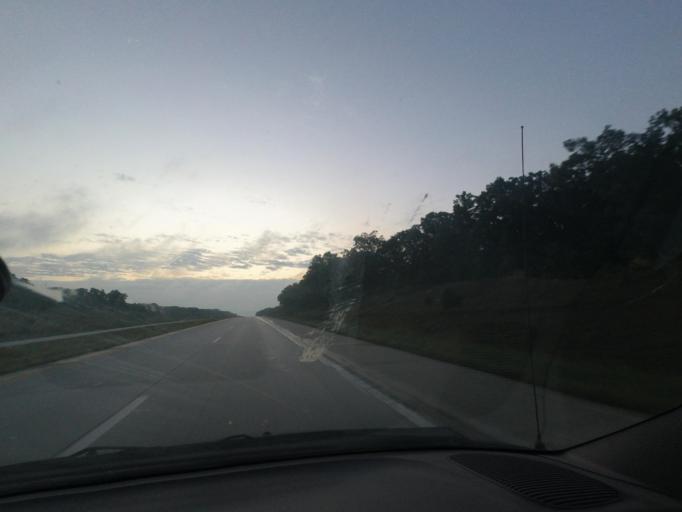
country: US
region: Missouri
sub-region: Linn County
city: Marceline
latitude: 39.7590
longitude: -92.8481
